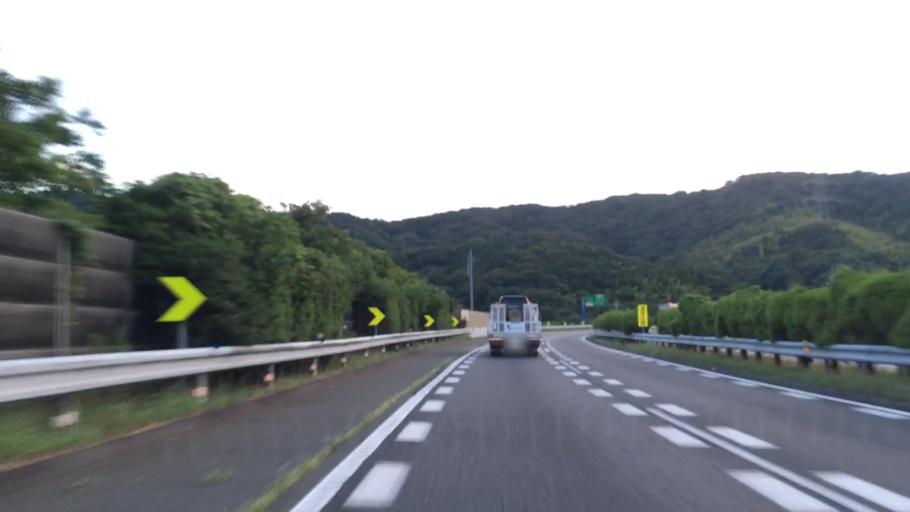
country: JP
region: Yamaguchi
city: Shimonoseki
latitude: 33.9297
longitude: 130.9943
